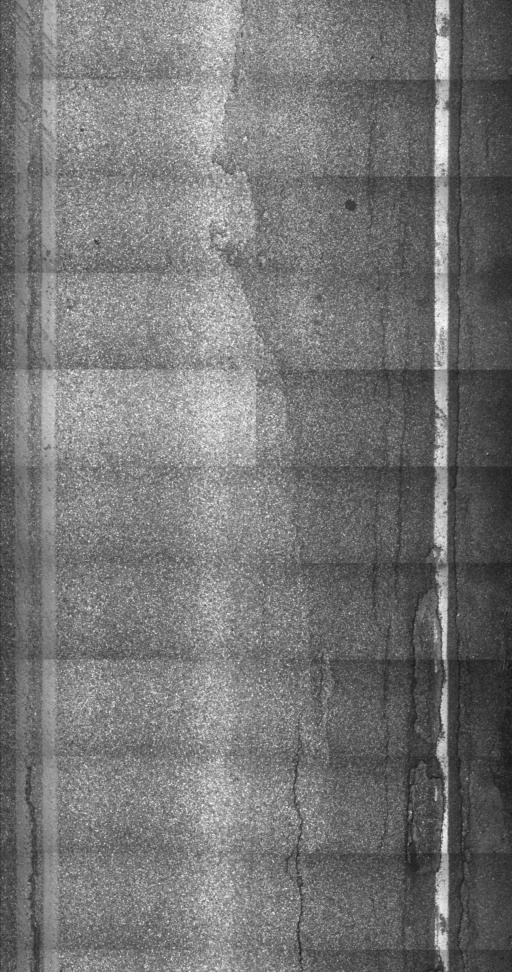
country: US
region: Vermont
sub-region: Bennington County
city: Manchester Center
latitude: 43.2499
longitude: -73.0934
